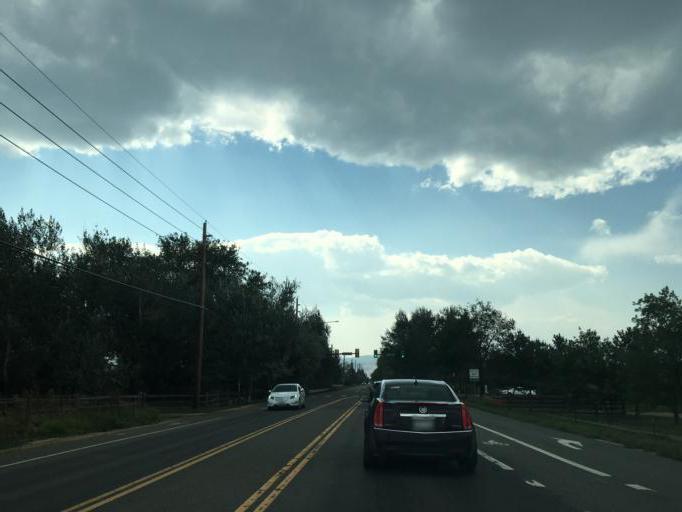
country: US
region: Colorado
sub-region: Boulder County
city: Gunbarrel
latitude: 40.0510
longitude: -105.2148
